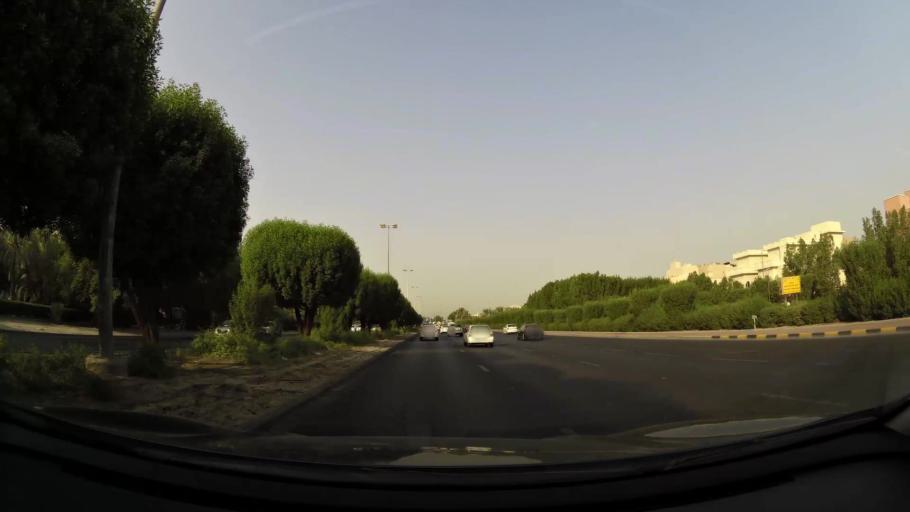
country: KW
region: Al Asimah
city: Ash Shamiyah
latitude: 29.3193
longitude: 47.9812
